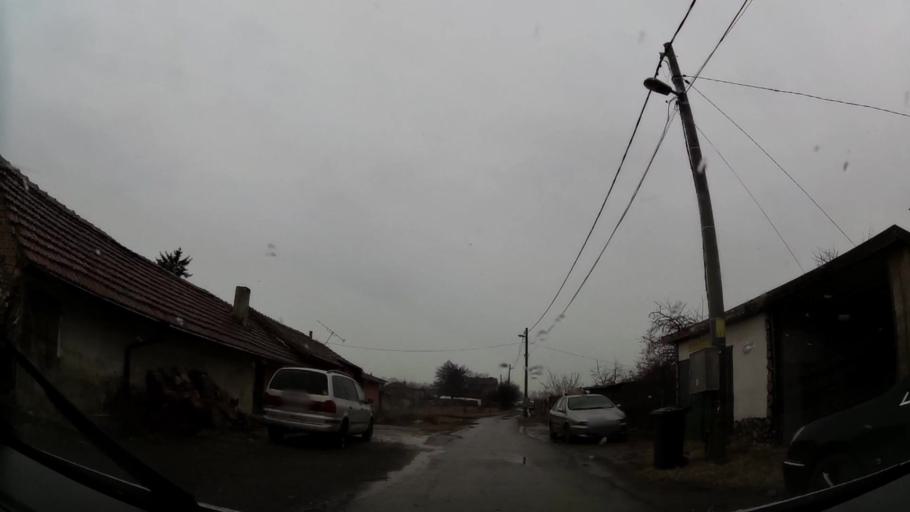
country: BG
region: Sofia-Capital
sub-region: Stolichna Obshtina
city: Sofia
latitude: 42.6654
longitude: 23.4281
